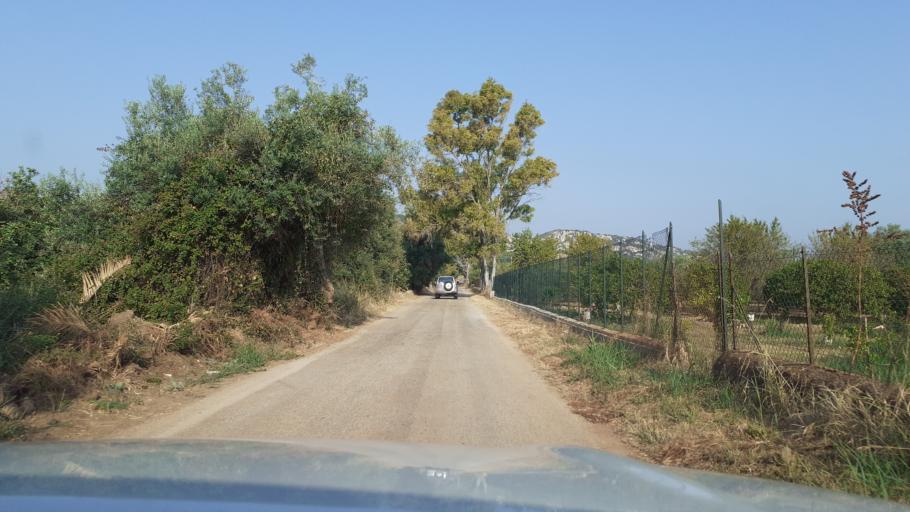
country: IT
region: Sicily
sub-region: Provincia di Siracusa
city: Cassibile
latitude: 36.9749
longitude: 15.1866
